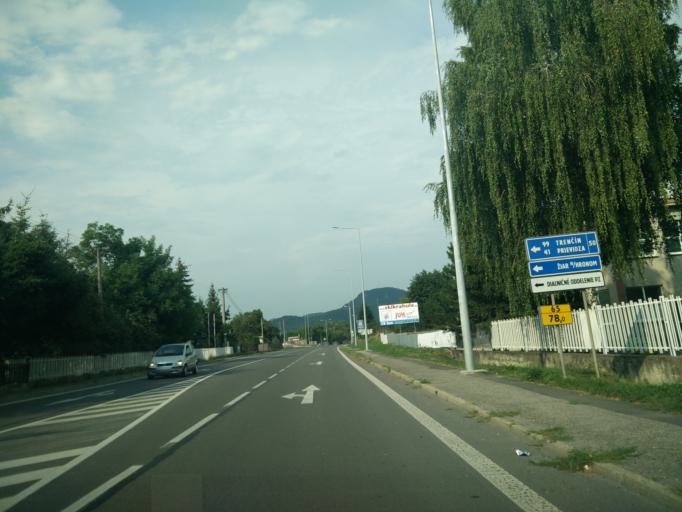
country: SK
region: Banskobystricky
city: Ziar nad Hronom
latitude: 48.5775
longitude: 18.8719
